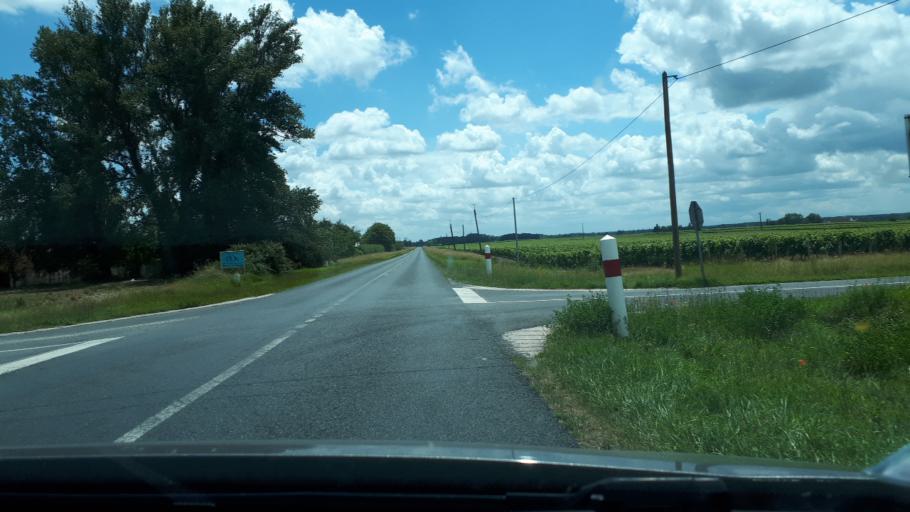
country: FR
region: Centre
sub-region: Departement du Loir-et-Cher
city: Contres
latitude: 47.3862
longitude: 1.4078
